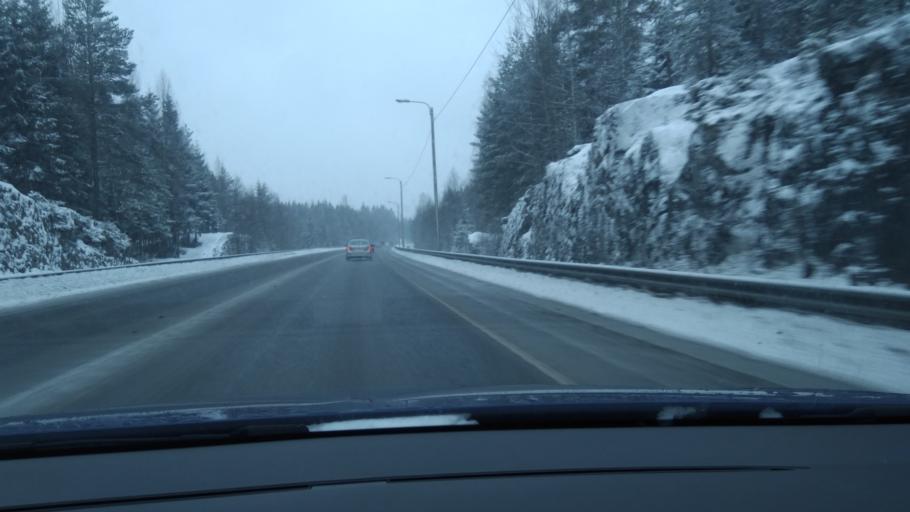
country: FI
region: Pirkanmaa
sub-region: Tampere
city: Tampere
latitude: 61.5112
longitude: 23.9108
